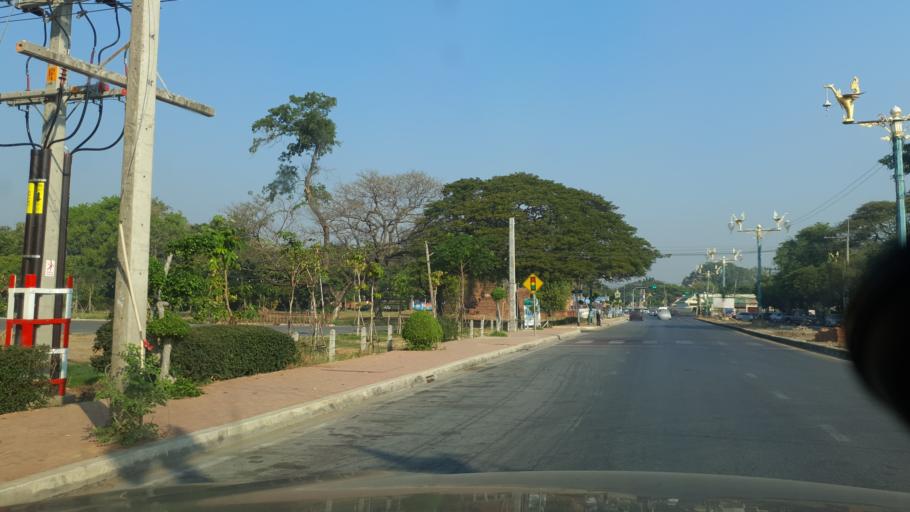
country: TH
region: Phra Nakhon Si Ayutthaya
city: Phra Nakhon Si Ayutthaya
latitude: 14.3594
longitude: 100.5685
